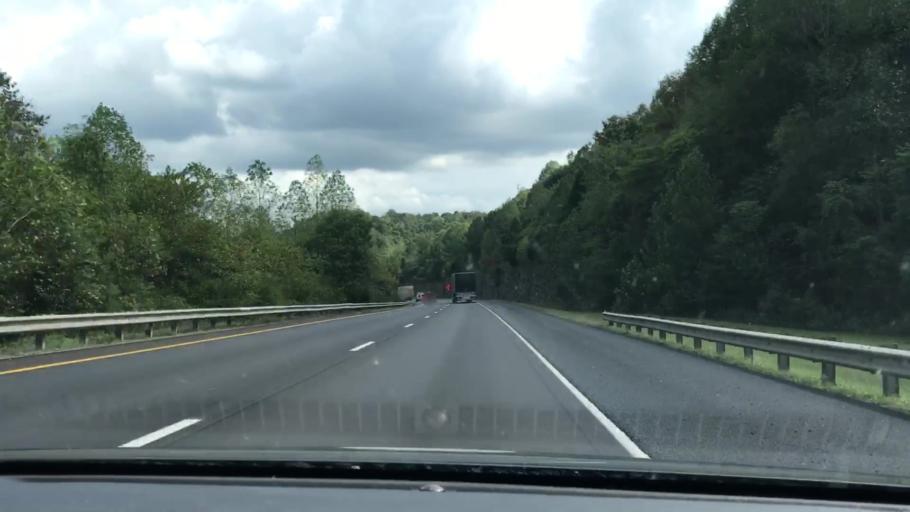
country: US
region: Tennessee
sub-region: Robertson County
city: Ridgetop
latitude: 36.3195
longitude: -86.8486
